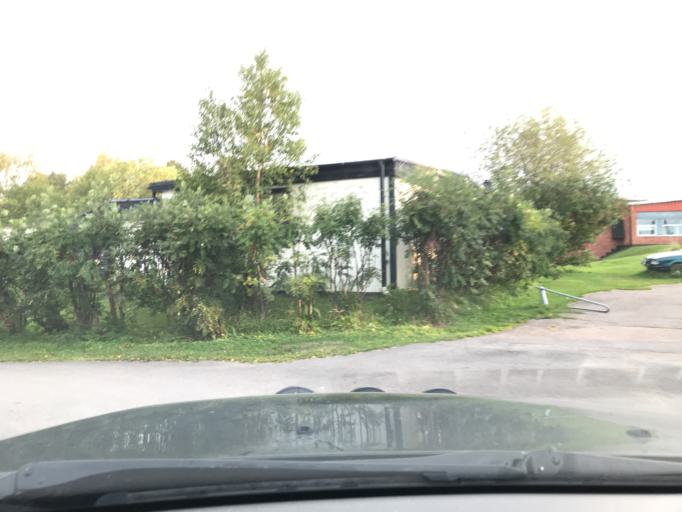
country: SE
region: Norrbotten
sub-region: Gallivare Kommun
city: Malmberget
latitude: 67.6488
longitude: 21.0529
